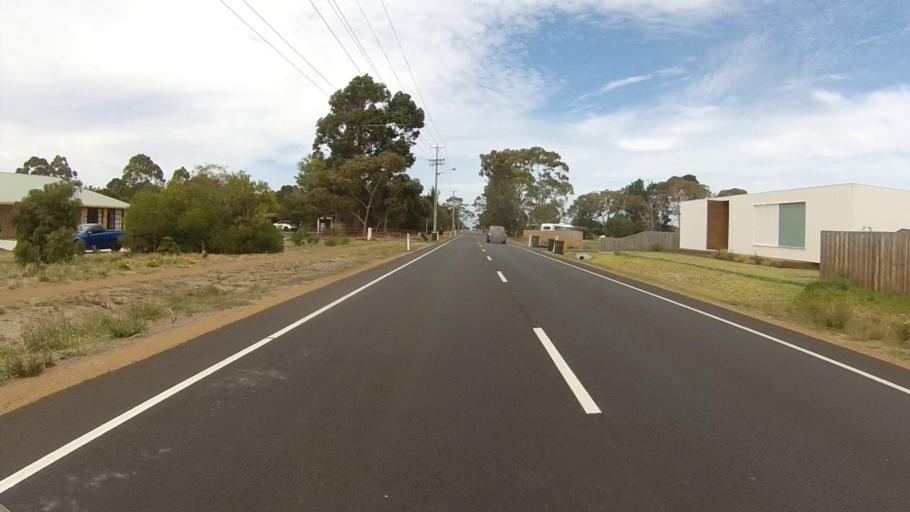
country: AU
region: Tasmania
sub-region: Clarence
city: Seven Mile Beach
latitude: -42.8622
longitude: 147.4991
